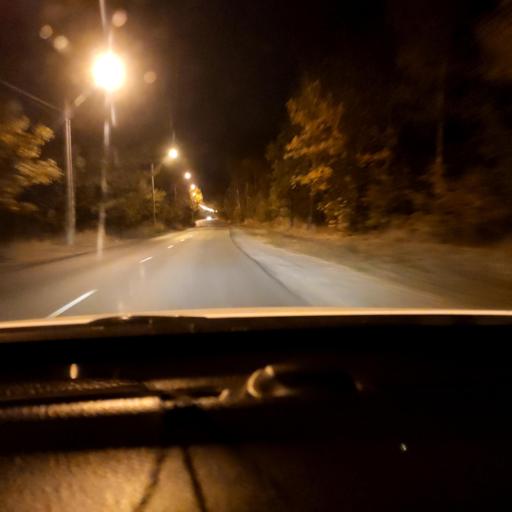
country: RU
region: Voronezj
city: Somovo
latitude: 51.7138
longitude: 39.3259
